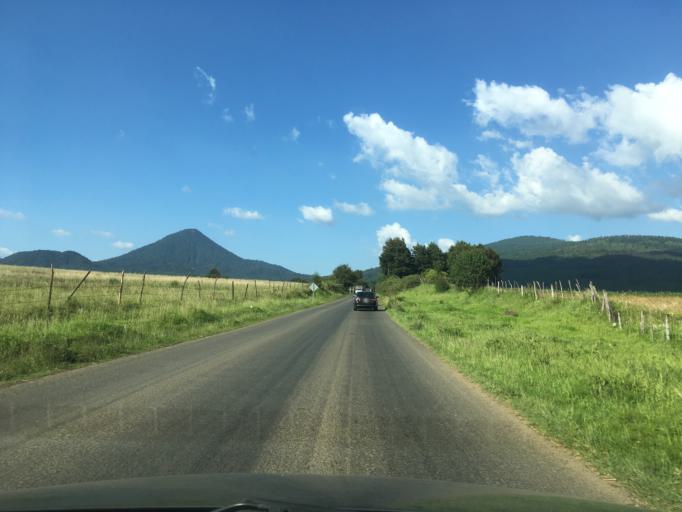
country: MX
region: Michoacan
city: Nahuatzen
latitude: 19.6452
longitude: -101.9223
